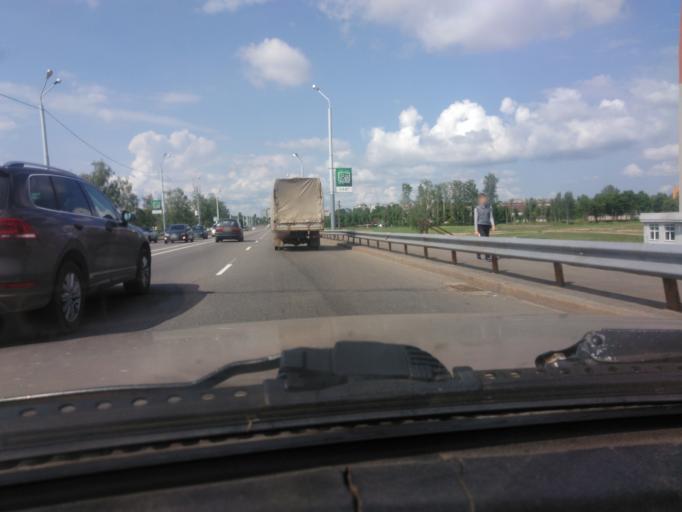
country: BY
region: Mogilev
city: Mahilyow
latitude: 53.9226
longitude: 30.3497
